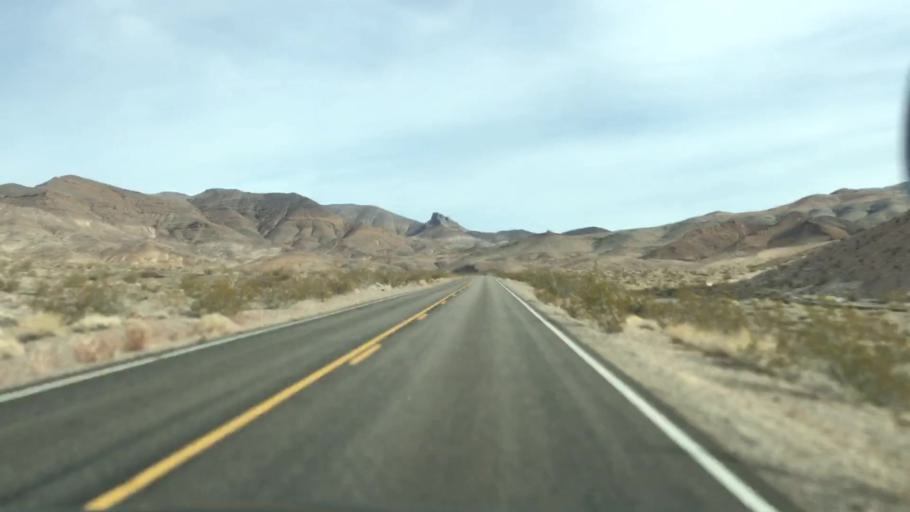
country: US
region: Nevada
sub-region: Nye County
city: Beatty
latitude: 36.7273
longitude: -116.9754
